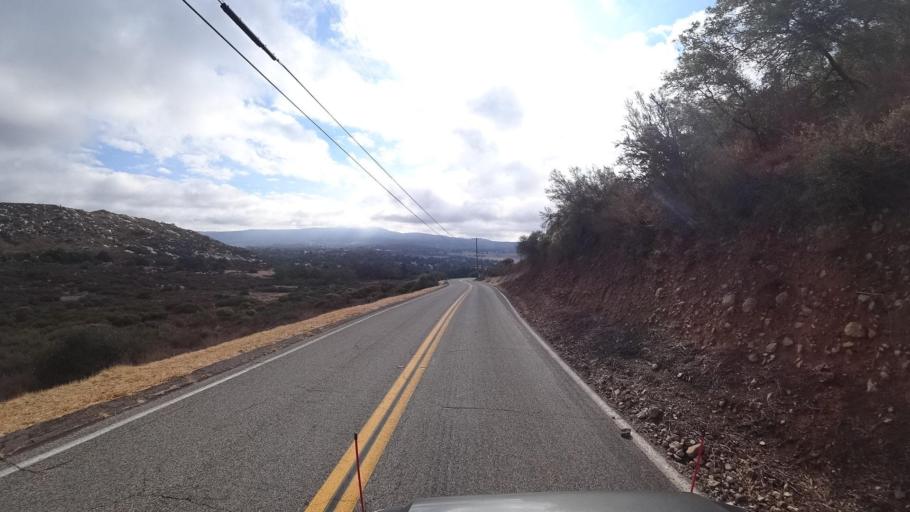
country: MX
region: Baja California
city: Tecate
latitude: 32.6259
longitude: -116.6266
